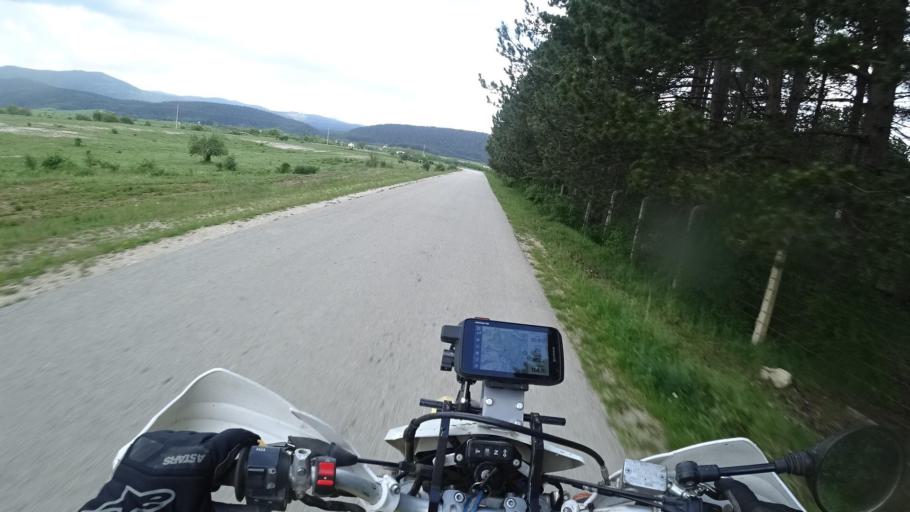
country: BA
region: Federation of Bosnia and Herzegovina
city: Glamoc
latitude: 44.0729
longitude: 16.8225
